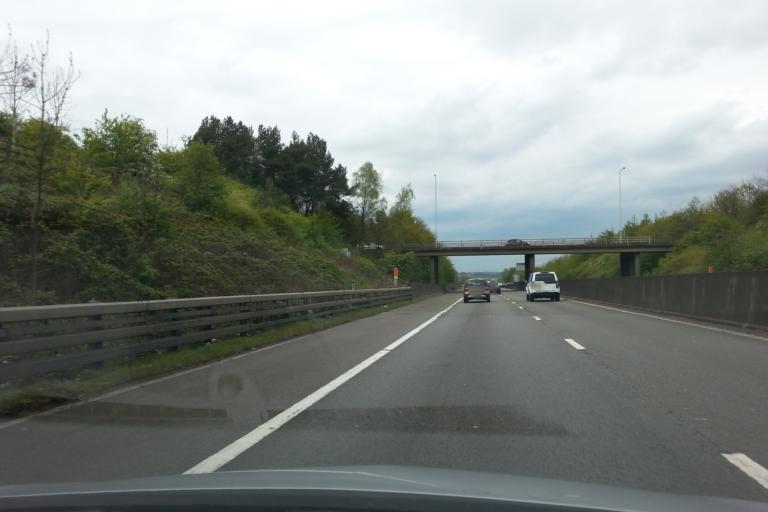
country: GB
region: England
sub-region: Leicestershire
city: Donisthorpe
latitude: 52.6887
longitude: -1.5485
